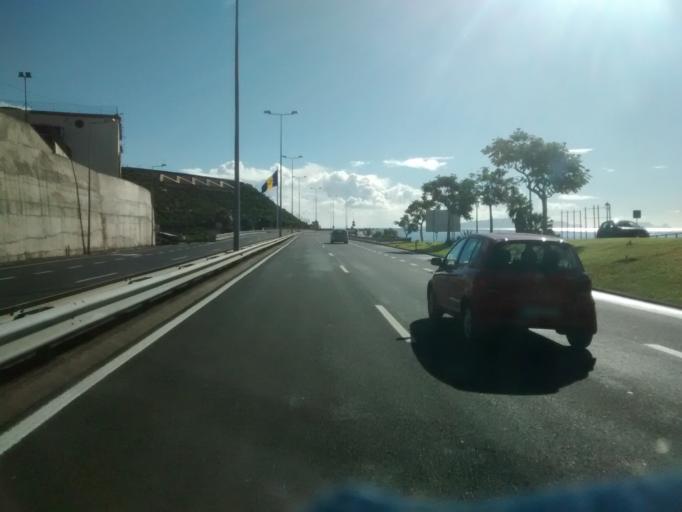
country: PT
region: Madeira
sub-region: Santa Cruz
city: Santa Cruz
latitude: 32.6891
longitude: -16.7879
